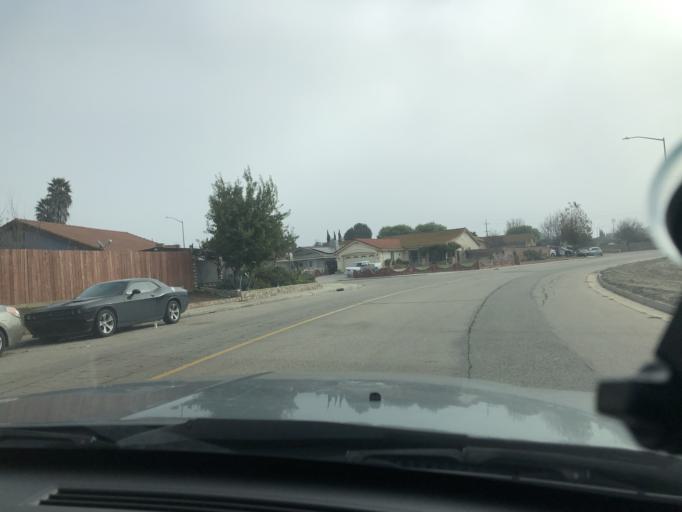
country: US
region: California
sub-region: Monterey County
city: King City
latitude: 36.2124
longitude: -121.1395
